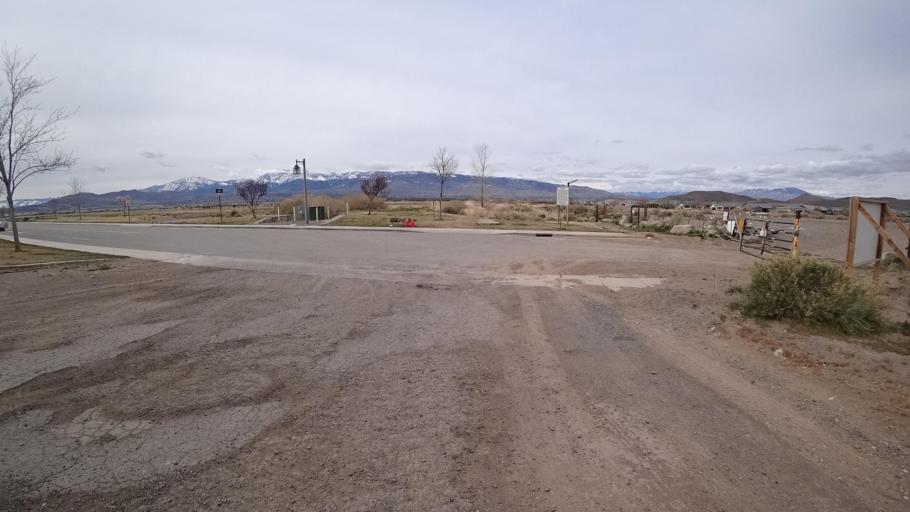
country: US
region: Nevada
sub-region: Washoe County
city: Sparks
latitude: 39.4407
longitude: -119.7152
